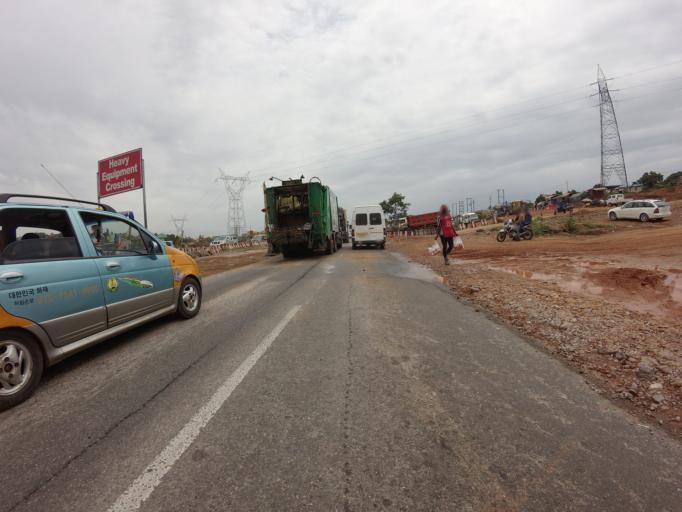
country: GH
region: Greater Accra
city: Dome
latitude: 5.6835
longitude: -0.2766
